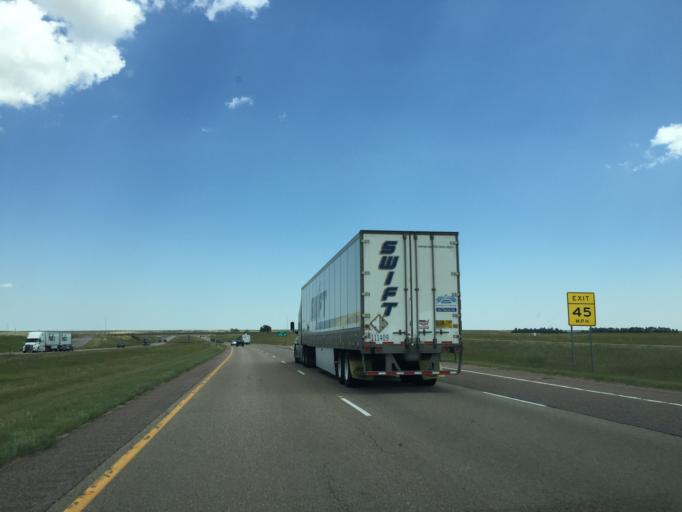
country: US
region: Colorado
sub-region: Lincoln County
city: Hugo
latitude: 39.2786
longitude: -103.4031
